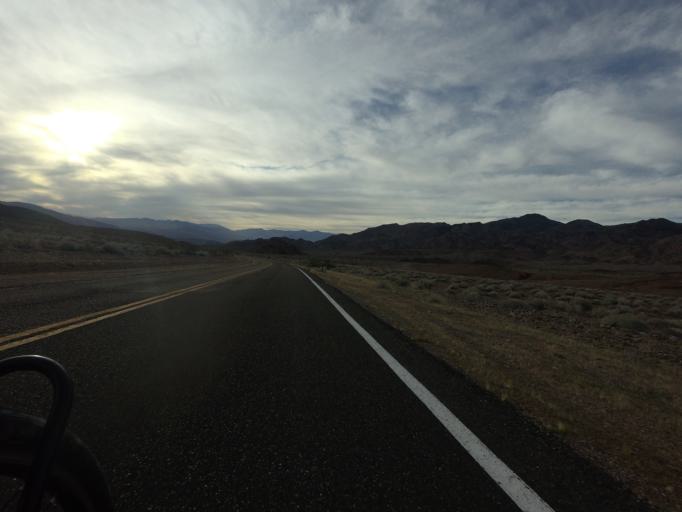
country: US
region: California
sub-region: San Bernardino County
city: Fort Irwin
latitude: 35.9121
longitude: -116.5855
